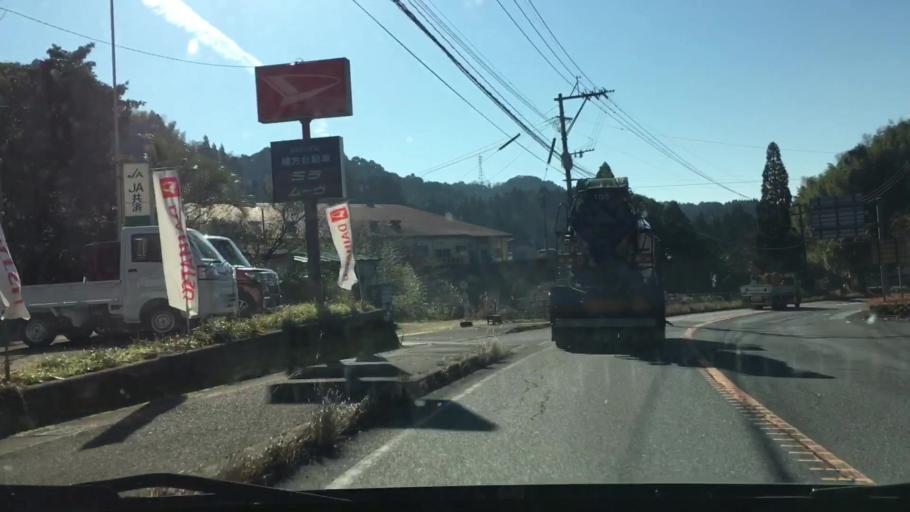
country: JP
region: Kagoshima
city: Kajiki
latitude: 31.7548
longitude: 130.6783
